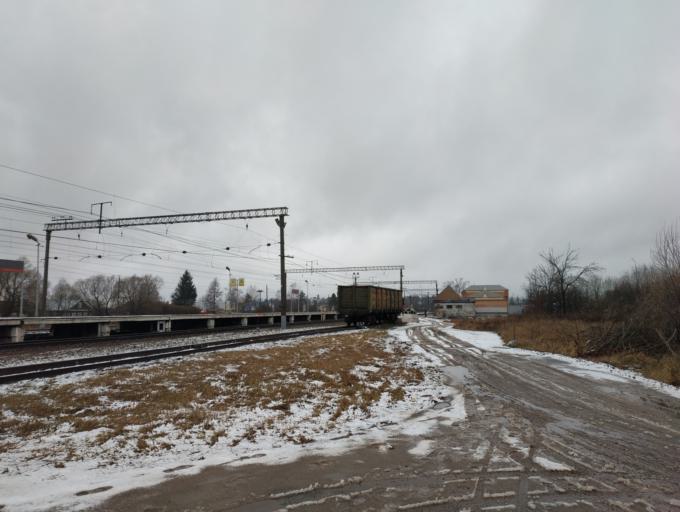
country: RU
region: Moskovskaya
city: Taldom
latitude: 56.7215
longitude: 37.5286
